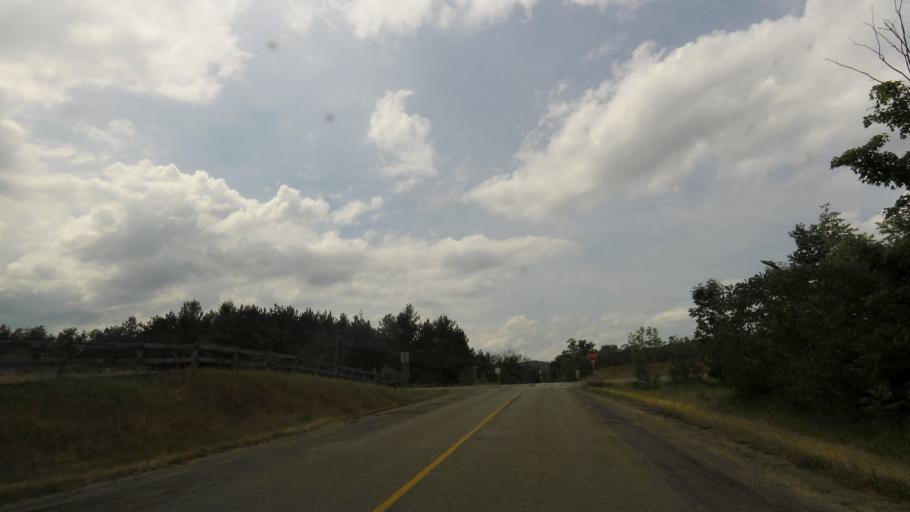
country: CA
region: Ontario
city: Orangeville
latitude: 43.8592
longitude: -79.8985
